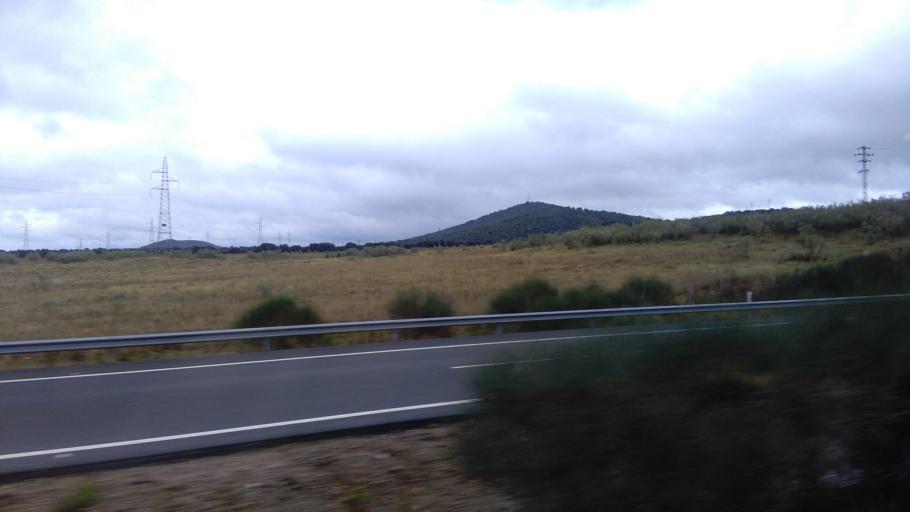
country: ES
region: Extremadura
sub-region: Provincia de Caceres
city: Almaraz
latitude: 39.8195
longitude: -5.6624
